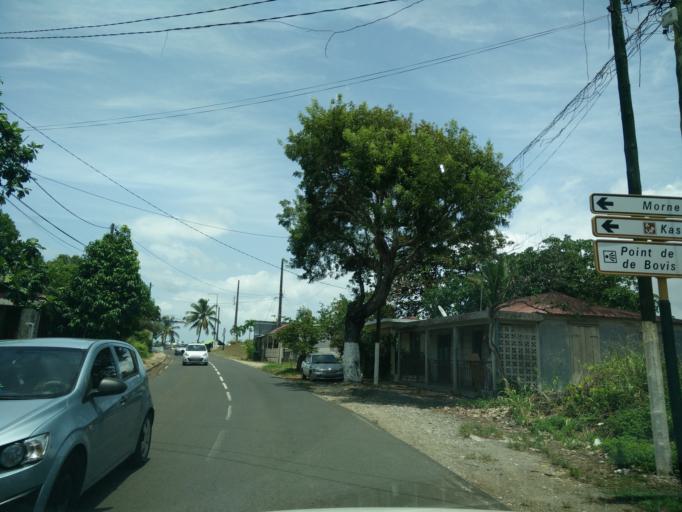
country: GP
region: Guadeloupe
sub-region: Guadeloupe
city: Petit-Bourg
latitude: 16.1876
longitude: -61.5898
